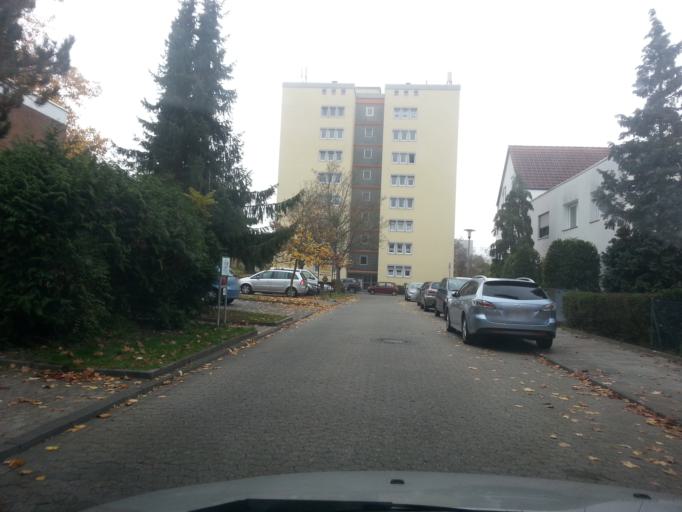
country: DE
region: Hesse
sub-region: Regierungsbezirk Darmstadt
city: Darmstadt
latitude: 49.9028
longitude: 8.6597
